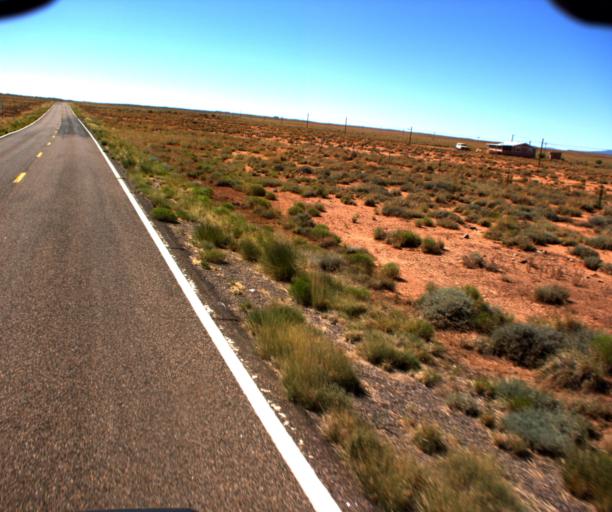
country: US
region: Arizona
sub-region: Coconino County
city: LeChee
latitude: 35.1350
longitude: -110.8855
